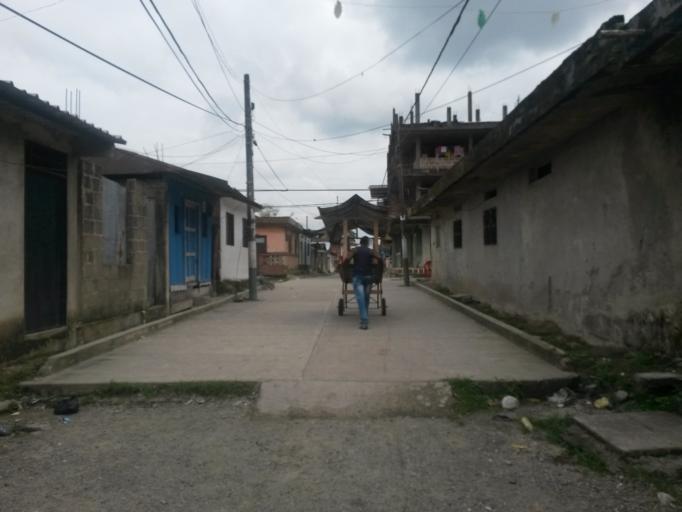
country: CO
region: Cauca
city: Guapi
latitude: 2.5714
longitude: -77.8853
